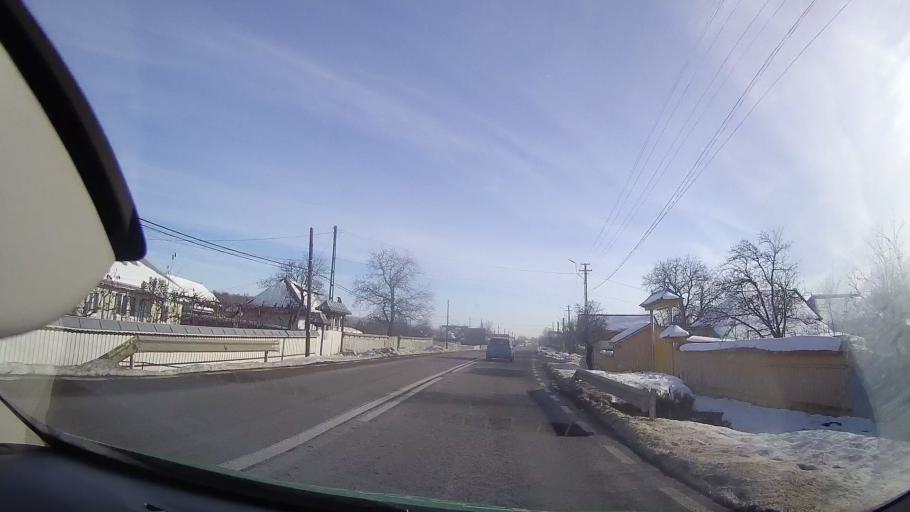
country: RO
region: Neamt
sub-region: Comuna Cracaoani
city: Cracaoani
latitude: 47.0952
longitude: 26.3156
